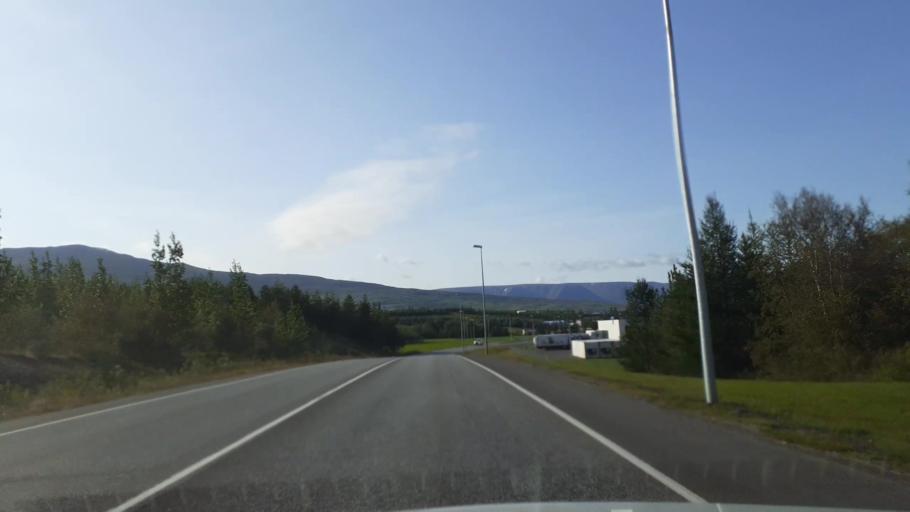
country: IS
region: Northeast
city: Akureyri
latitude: 65.6735
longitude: -18.1253
